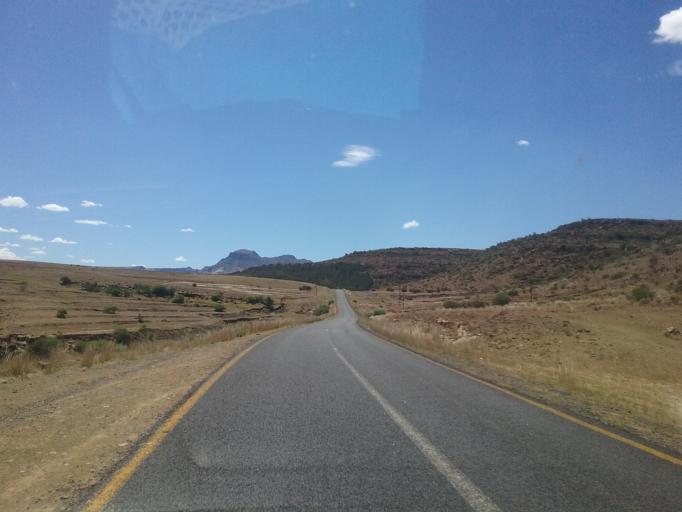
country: LS
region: Quthing
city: Quthing
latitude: -30.2868
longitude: 27.7812
